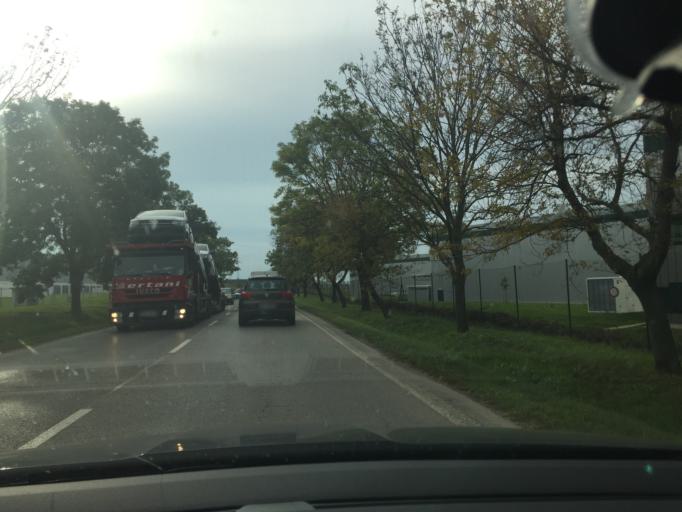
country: CZ
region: Central Bohemia
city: Jirny
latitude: 50.1247
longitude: 14.6874
